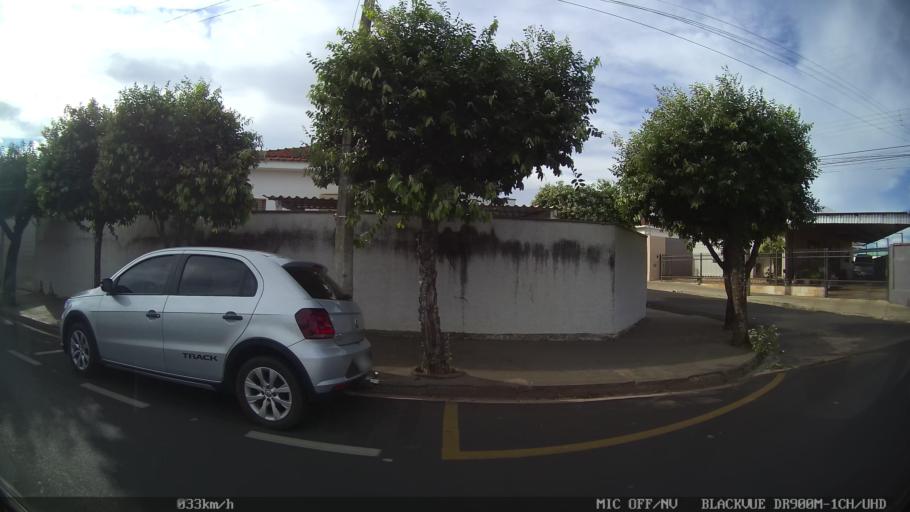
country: BR
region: Sao Paulo
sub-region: Catanduva
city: Catanduva
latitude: -21.1208
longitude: -48.9664
